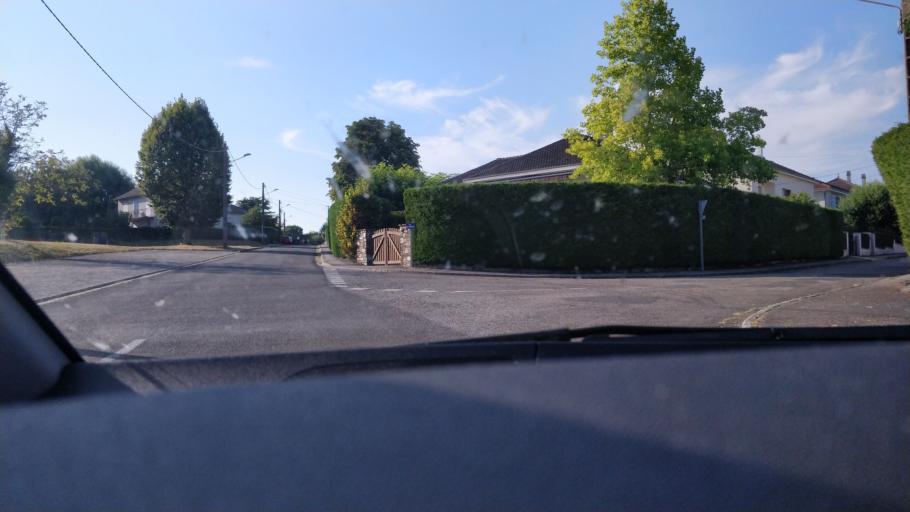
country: FR
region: Limousin
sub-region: Departement de la Haute-Vienne
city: Couzeix
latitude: 45.8827
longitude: 1.2420
